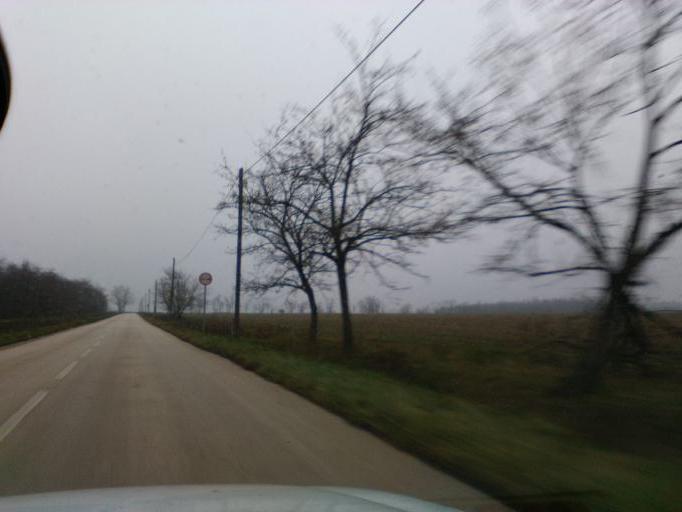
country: HU
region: Pest
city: Soskut
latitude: 47.3876
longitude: 18.7933
